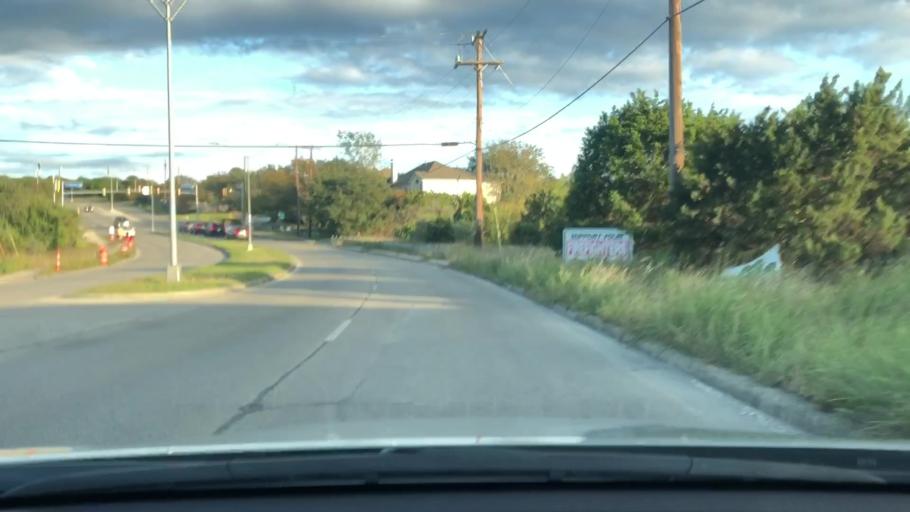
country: US
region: Texas
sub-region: Bexar County
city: Hollywood Park
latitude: 29.6345
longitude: -98.5161
